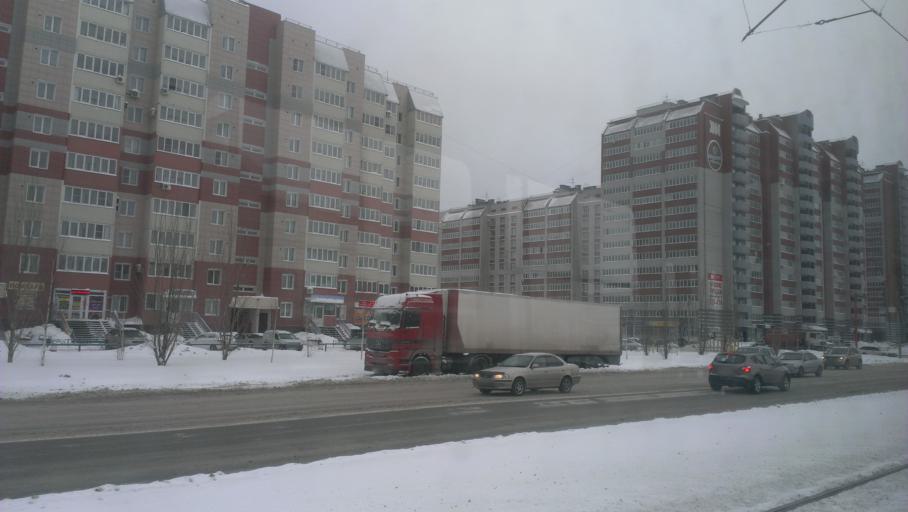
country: RU
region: Altai Krai
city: Novosilikatnyy
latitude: 53.3289
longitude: 83.6769
